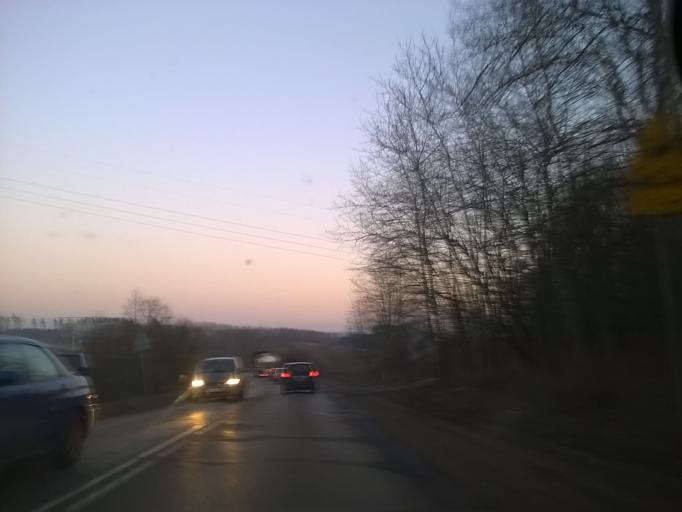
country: PL
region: Warmian-Masurian Voivodeship
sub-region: Powiat olsztynski
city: Olsztyn
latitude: 53.7793
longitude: 20.5555
